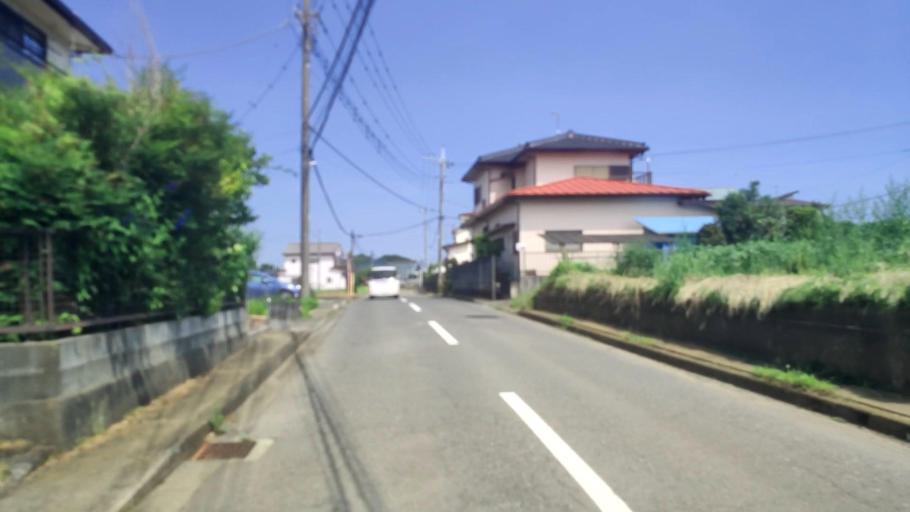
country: JP
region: Kanagawa
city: Hadano
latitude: 35.3572
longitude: 139.2500
